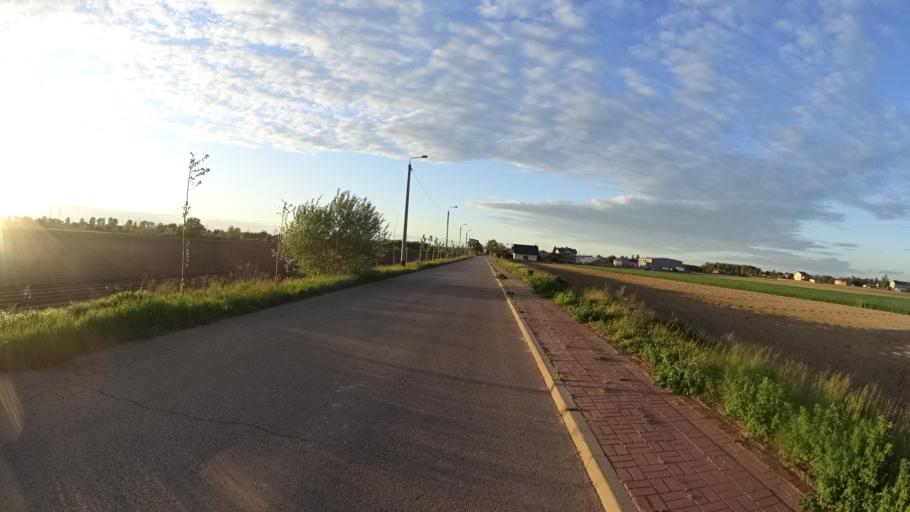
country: PL
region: Masovian Voivodeship
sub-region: Powiat warszawski zachodni
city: Jozefow
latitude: 52.2032
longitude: 20.7445
